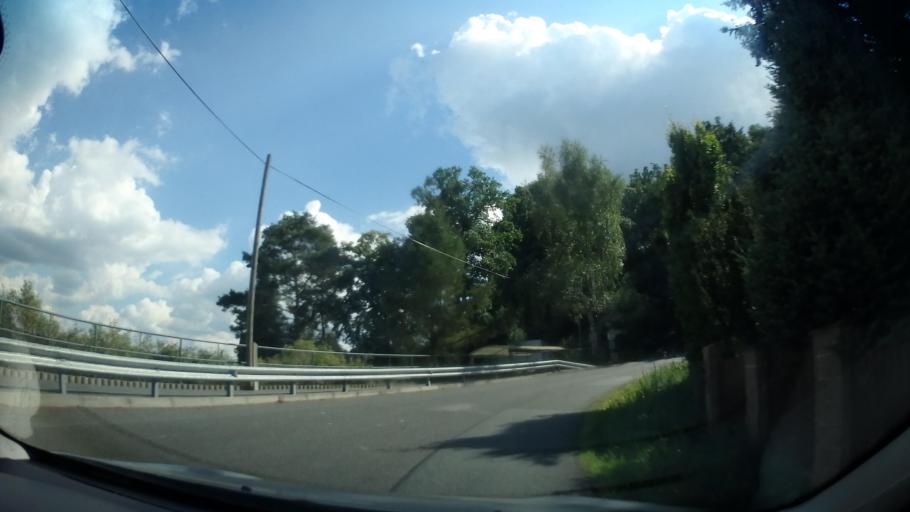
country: CZ
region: Central Bohemia
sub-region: Okres Praha-Vychod
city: Mnichovice
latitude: 49.9070
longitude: 14.7173
